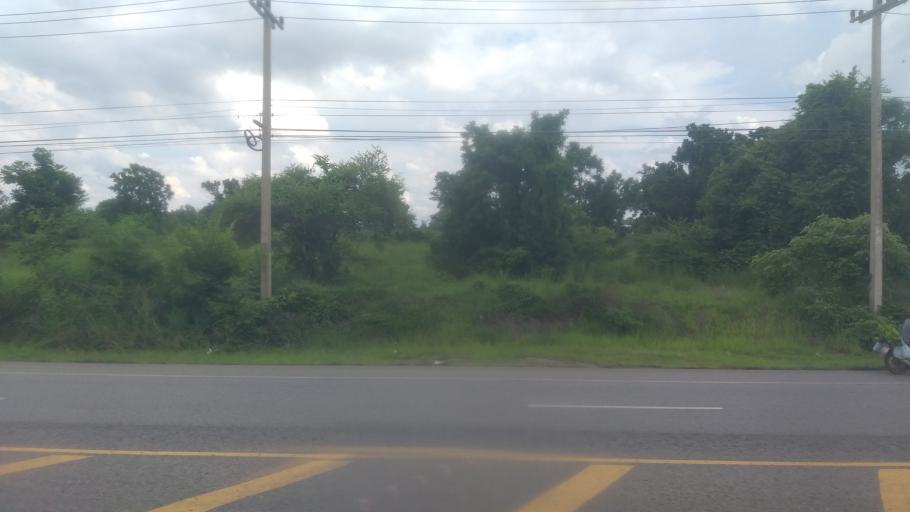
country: TH
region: Chaiyaphum
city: Noen Sa-nga
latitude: 15.6755
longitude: 101.9696
